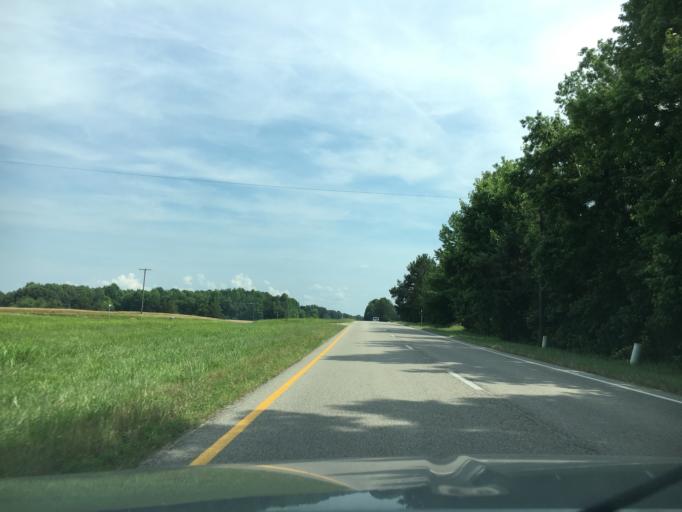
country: US
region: Virginia
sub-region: Nottoway County
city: Crewe
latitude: 37.2345
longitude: -78.1460
